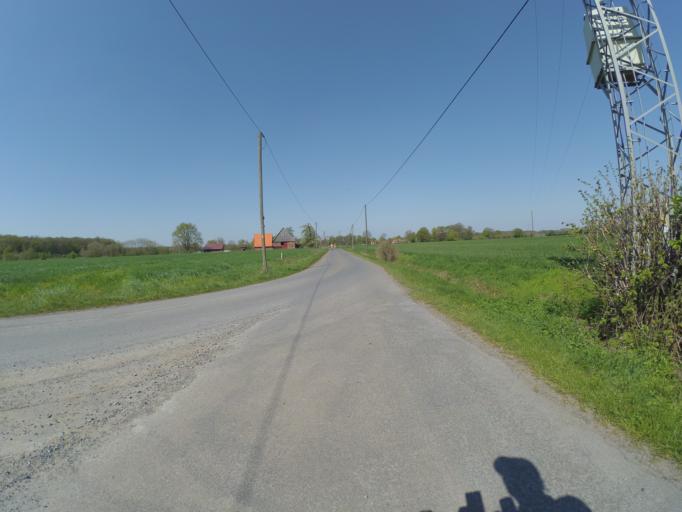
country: DE
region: North Rhine-Westphalia
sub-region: Regierungsbezirk Munster
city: Ascheberg
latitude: 51.8075
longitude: 7.5945
